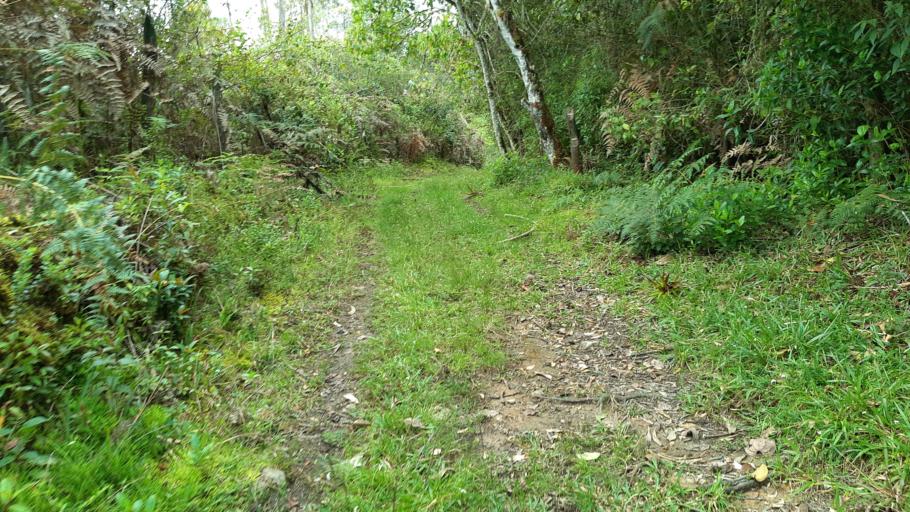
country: CO
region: Boyaca
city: Garagoa
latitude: 5.0835
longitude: -73.3172
